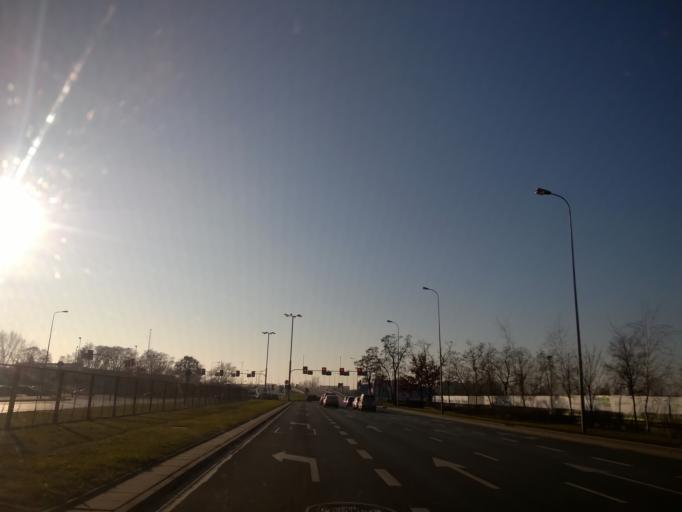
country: PL
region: Lower Silesian Voivodeship
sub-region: Powiat wroclawski
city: Wroclaw
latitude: 51.1205
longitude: 16.9727
